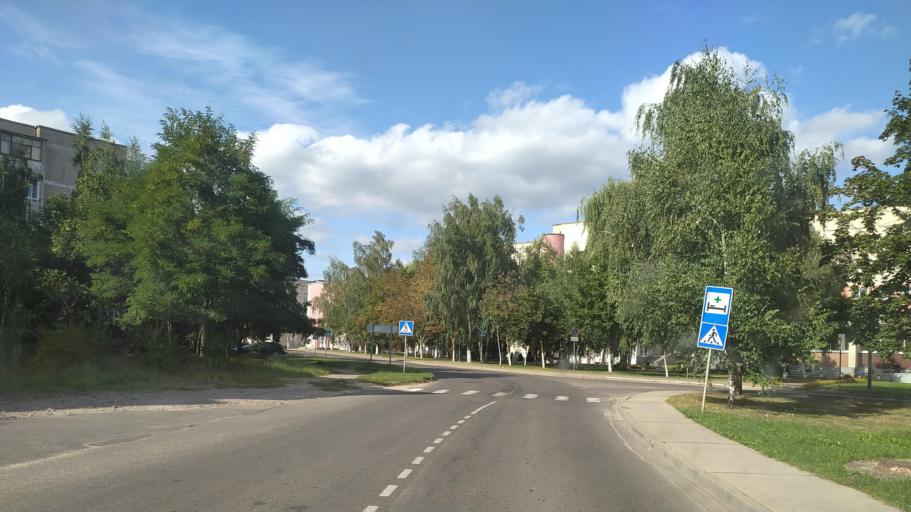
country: BY
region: Brest
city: Byaroza
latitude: 52.5369
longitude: 24.9961
